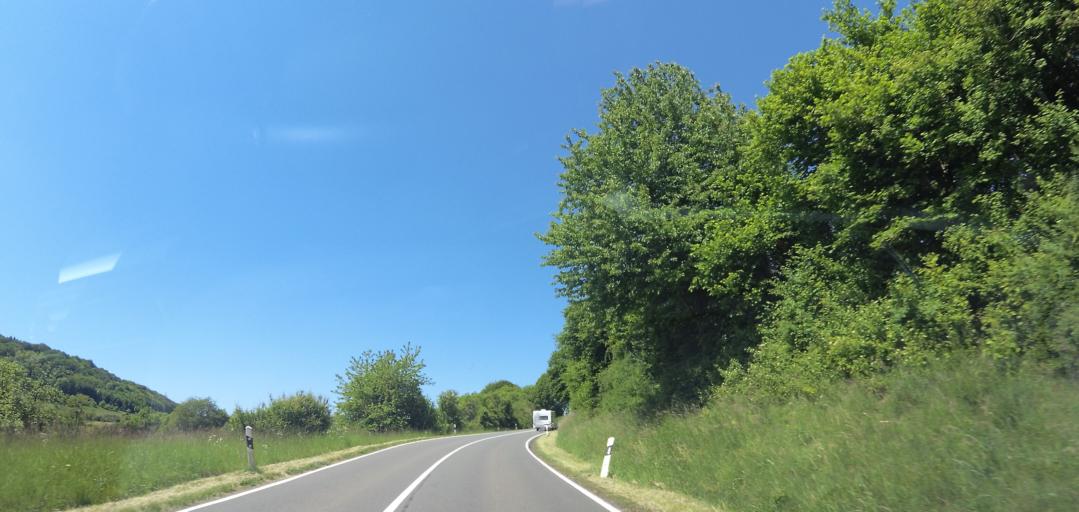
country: DE
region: Saarland
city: Losheim
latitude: 49.4616
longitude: 6.7213
